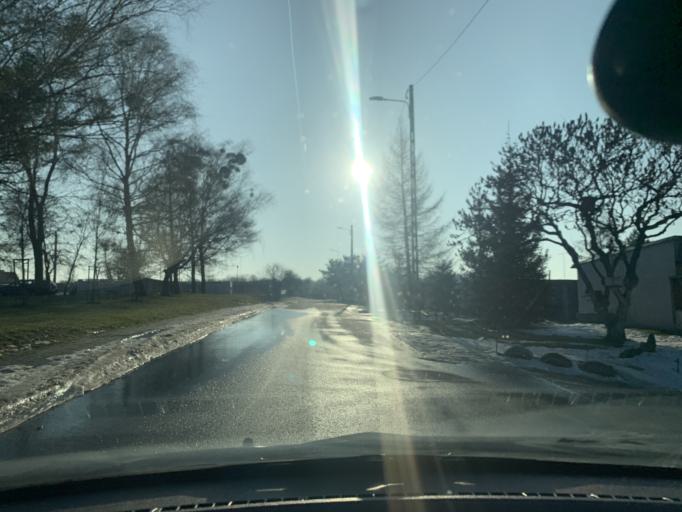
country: PL
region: Silesian Voivodeship
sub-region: Powiat tarnogorski
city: Radzionkow
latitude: 50.4062
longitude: 18.8952
